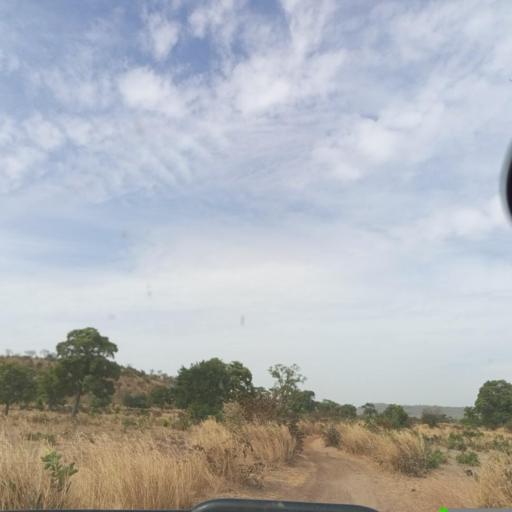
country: ML
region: Koulikoro
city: Koulikoro
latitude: 13.1744
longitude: -7.7391
